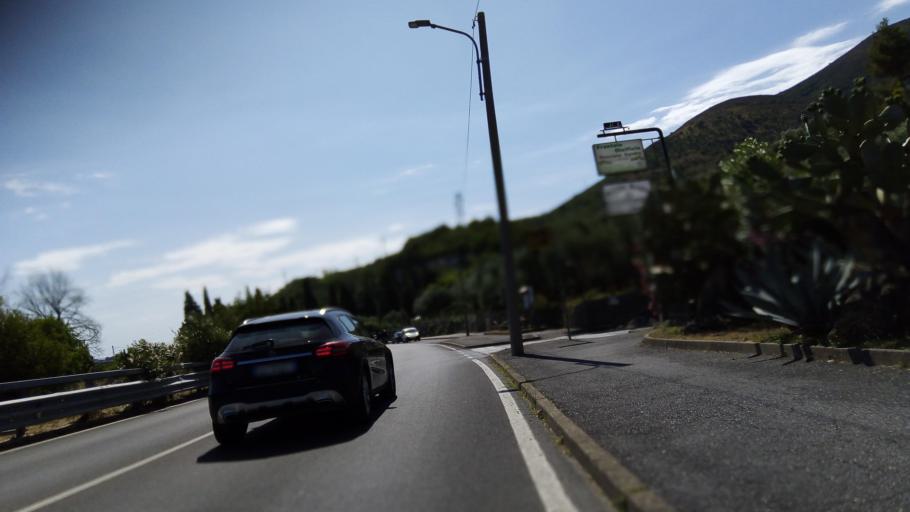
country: IT
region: Liguria
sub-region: Provincia di Savona
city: Toirano
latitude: 44.1225
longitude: 8.2142
